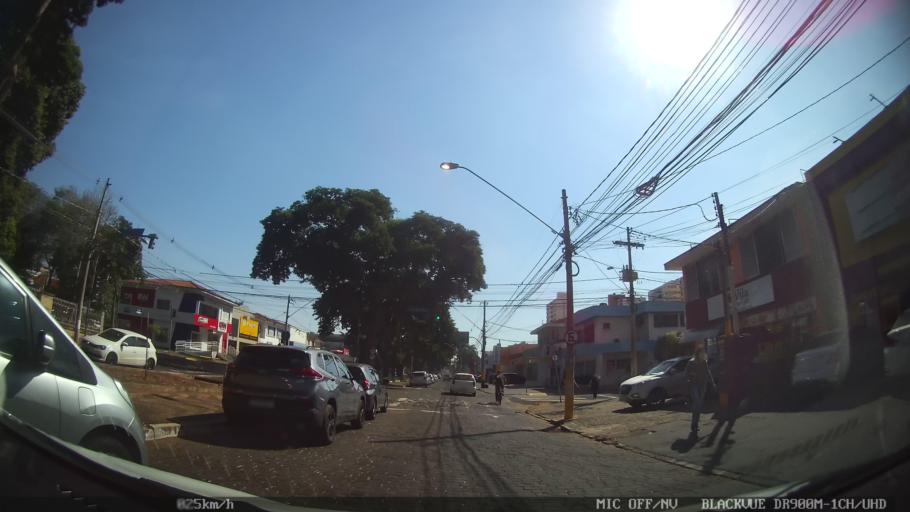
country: BR
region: Sao Paulo
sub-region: Ribeirao Preto
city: Ribeirao Preto
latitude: -21.1865
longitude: -47.8092
